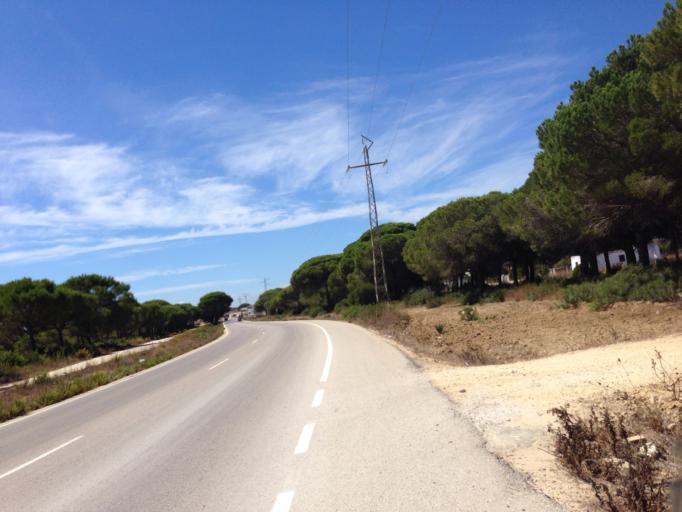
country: ES
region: Andalusia
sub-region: Provincia de Cadiz
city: Conil de la Frontera
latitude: 36.3315
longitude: -6.1219
